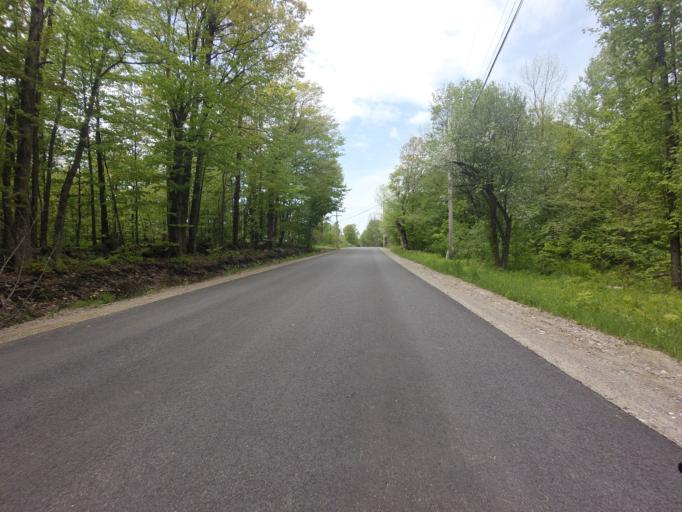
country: US
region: New York
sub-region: St. Lawrence County
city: Hannawa Falls
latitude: 44.5528
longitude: -74.9481
